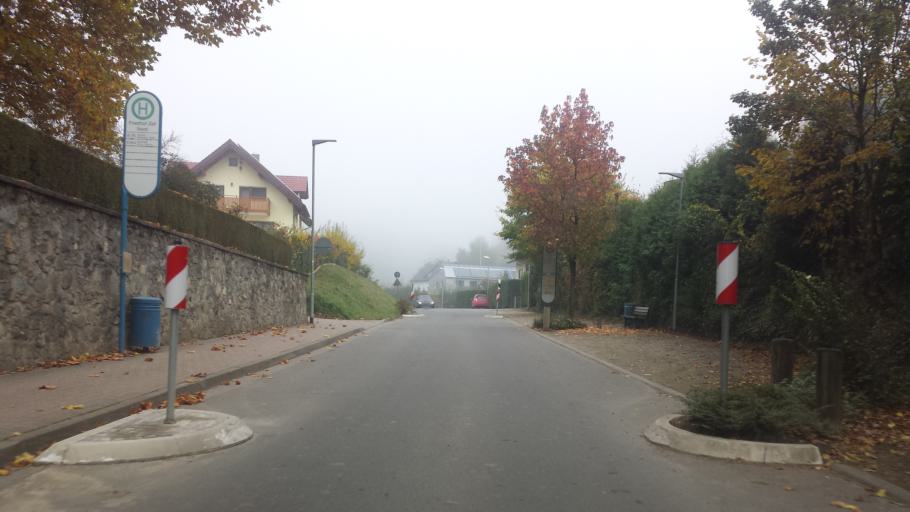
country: DE
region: Hesse
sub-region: Regierungsbezirk Darmstadt
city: Bensheim
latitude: 49.6764
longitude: 8.6562
